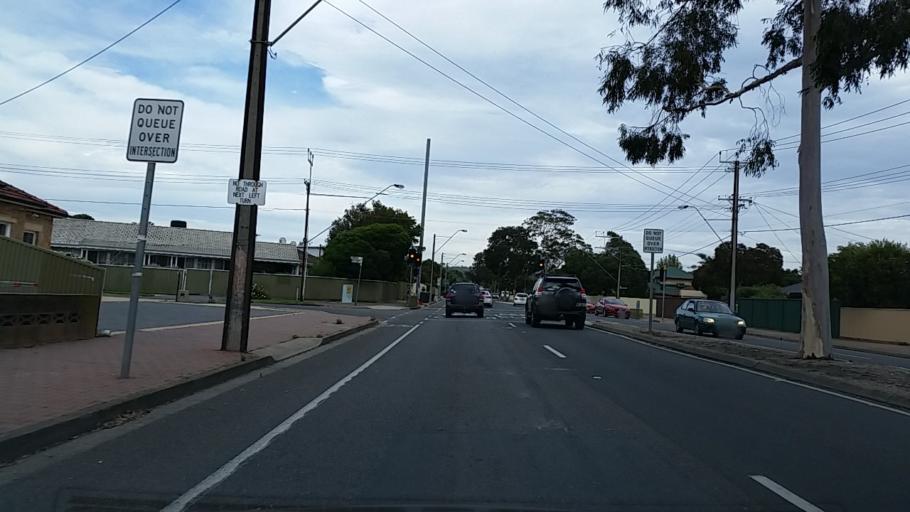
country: AU
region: South Australia
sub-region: Marion
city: Sturt
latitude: -35.0173
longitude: 138.5542
